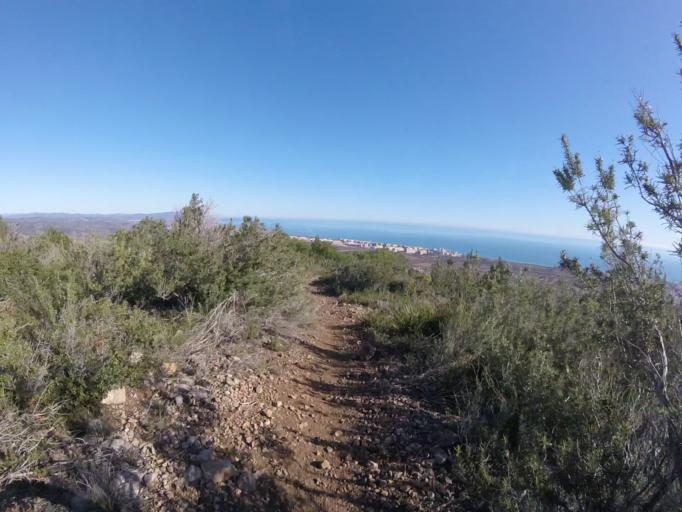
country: ES
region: Valencia
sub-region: Provincia de Castello
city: Orpesa/Oropesa del Mar
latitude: 40.1050
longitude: 0.1159
